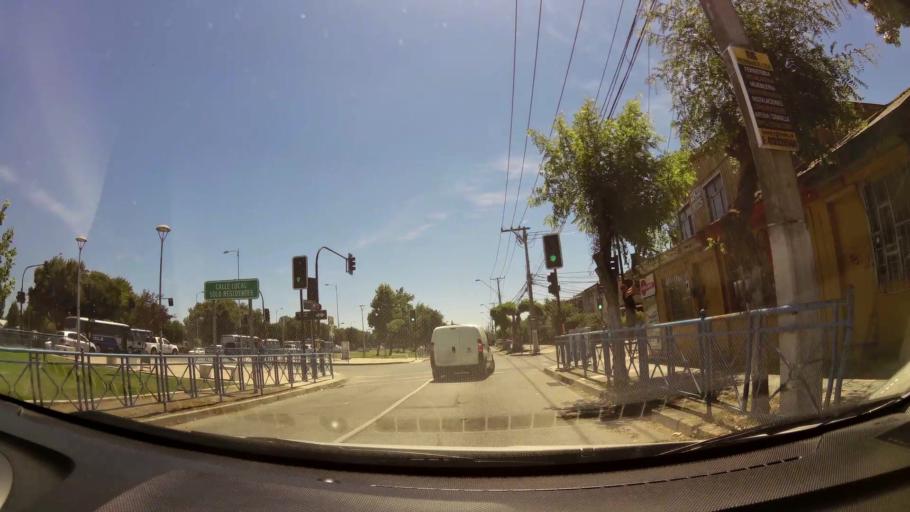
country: CL
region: Biobio
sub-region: Provincia de Concepcion
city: Talcahuano
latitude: -36.7603
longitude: -73.0888
